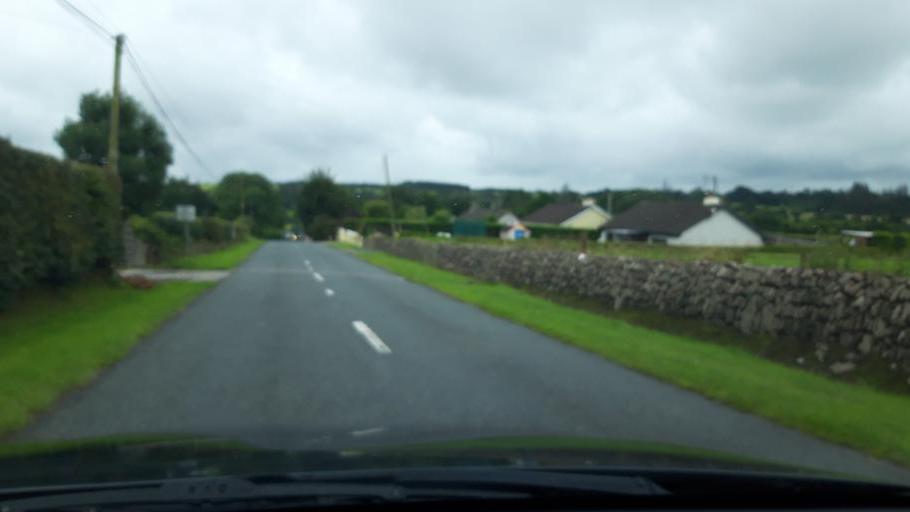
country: IE
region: Munster
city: Cahir
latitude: 52.1762
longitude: -7.8505
